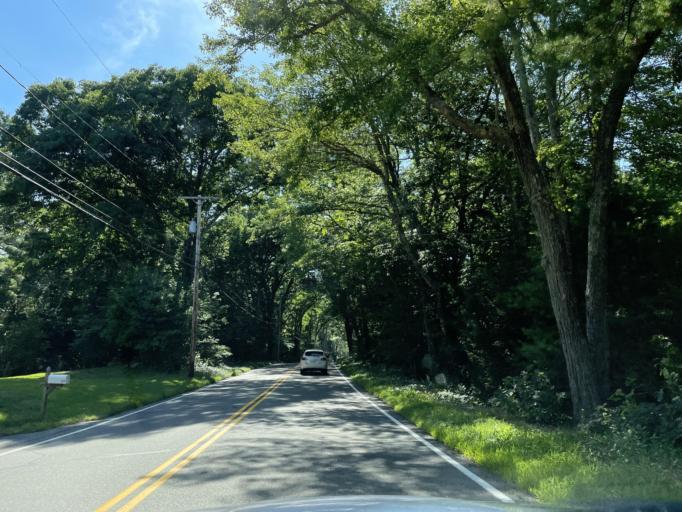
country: US
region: Massachusetts
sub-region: Worcester County
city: Sutton
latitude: 42.1511
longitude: -71.7120
